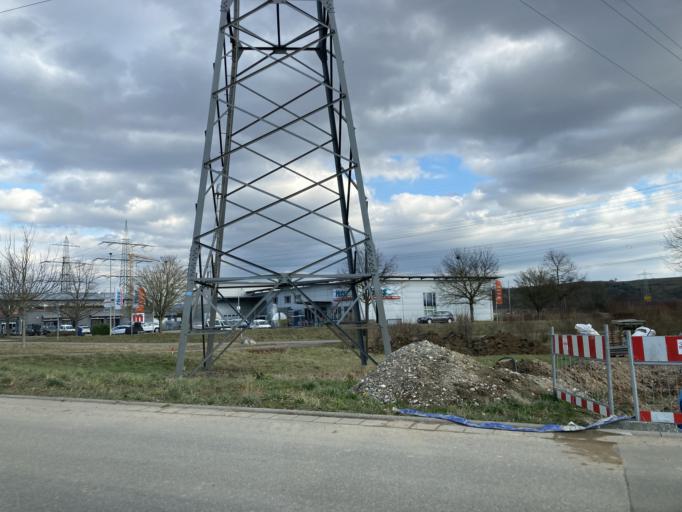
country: DE
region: Baden-Wuerttemberg
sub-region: Freiburg Region
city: Eichstetten
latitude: 48.0905
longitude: 7.7518
